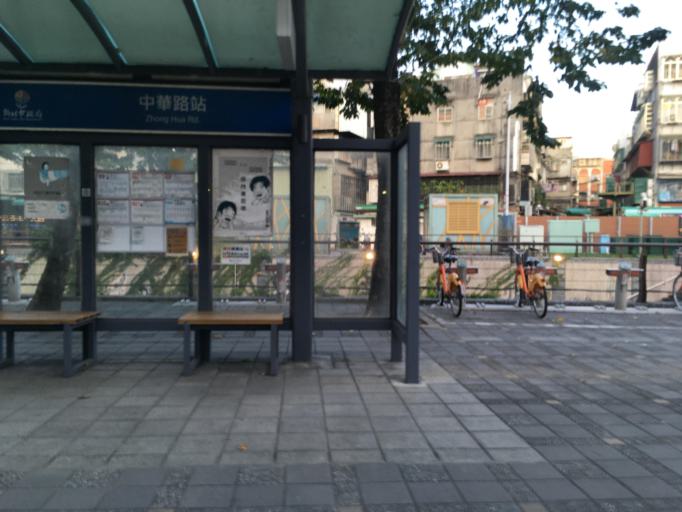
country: TW
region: Taipei
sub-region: Taipei
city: Banqiao
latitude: 25.0463
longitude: 121.4537
